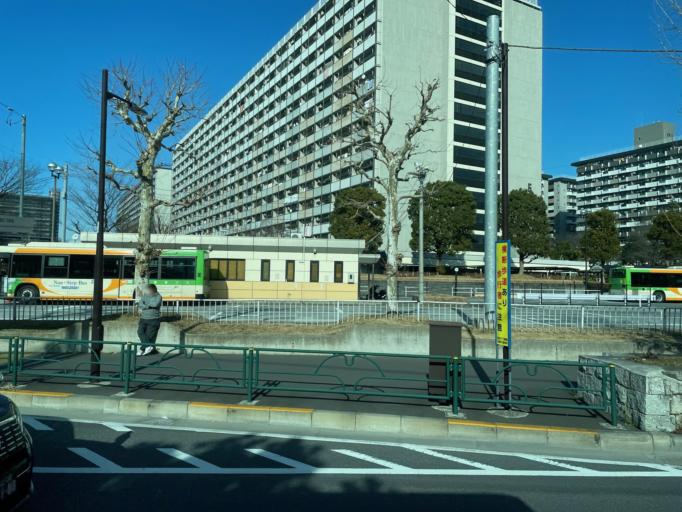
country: JP
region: Saitama
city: Kawaguchi
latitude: 35.7639
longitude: 139.7525
